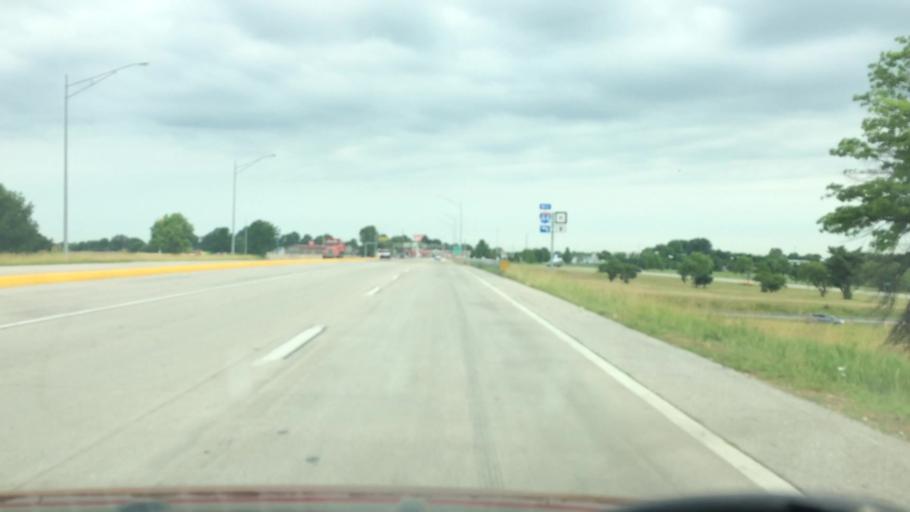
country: US
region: Missouri
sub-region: Greene County
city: Springfield
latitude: 37.2492
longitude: -93.2618
